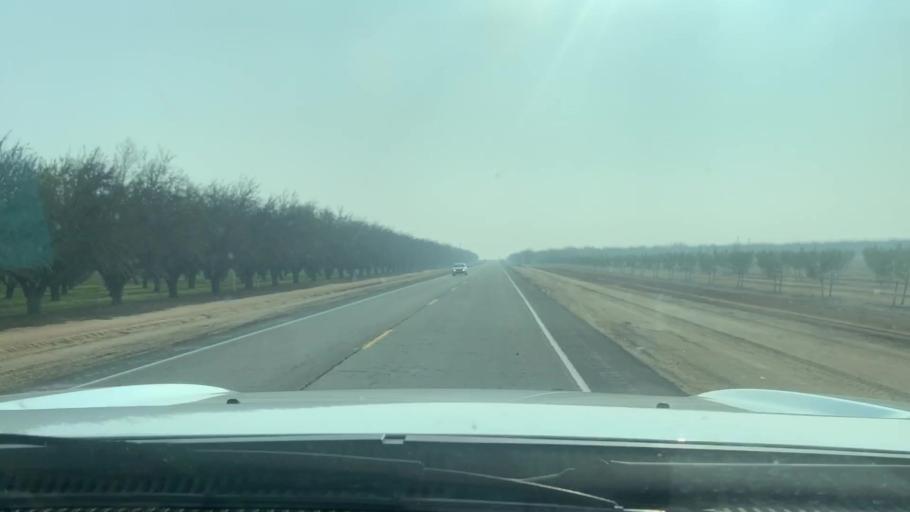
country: US
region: California
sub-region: Kern County
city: Rosedale
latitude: 35.4801
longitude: -119.1531
